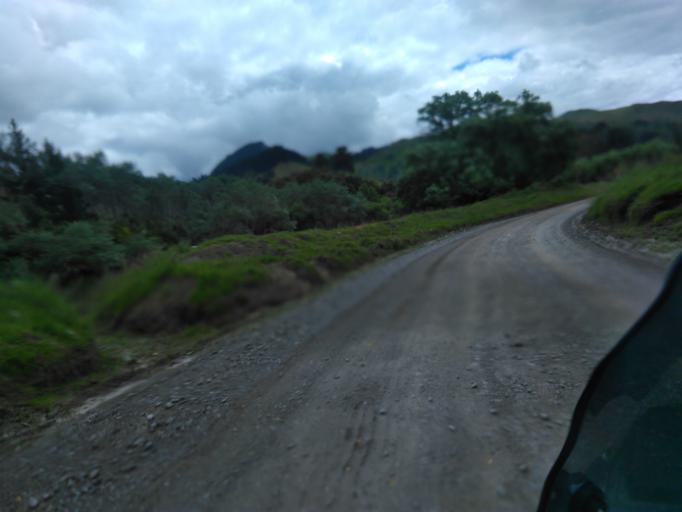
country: NZ
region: Gisborne
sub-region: Gisborne District
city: Gisborne
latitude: -38.0831
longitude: 178.0544
